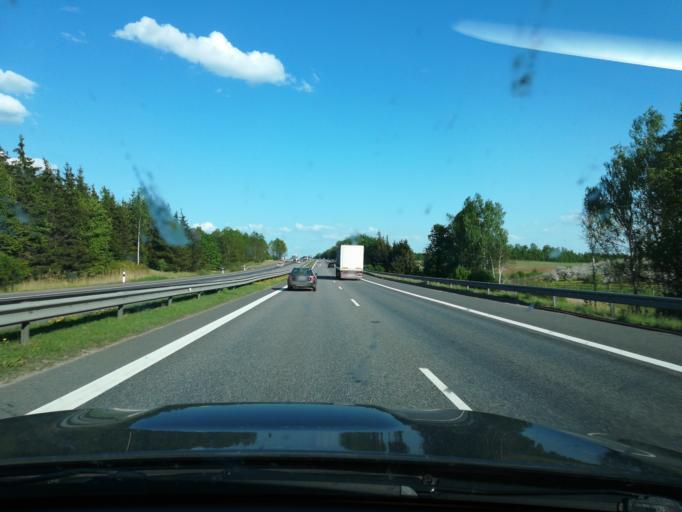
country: LT
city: Kaisiadorys
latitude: 54.8334
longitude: 24.3713
